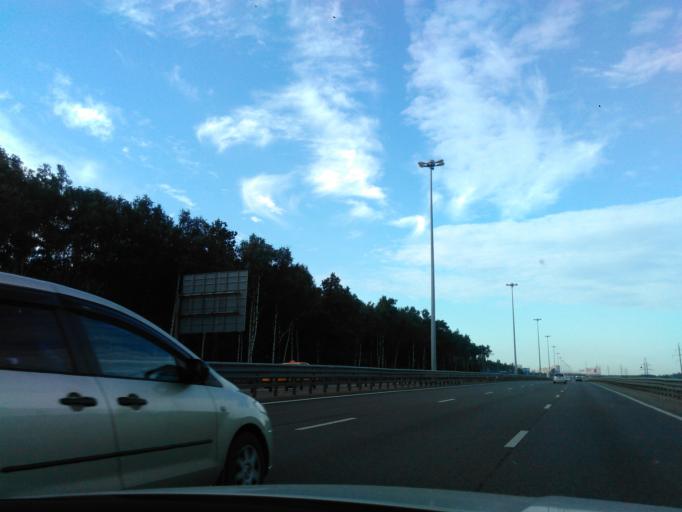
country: RU
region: Moscow
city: Khimki
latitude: 55.9440
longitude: 37.4089
